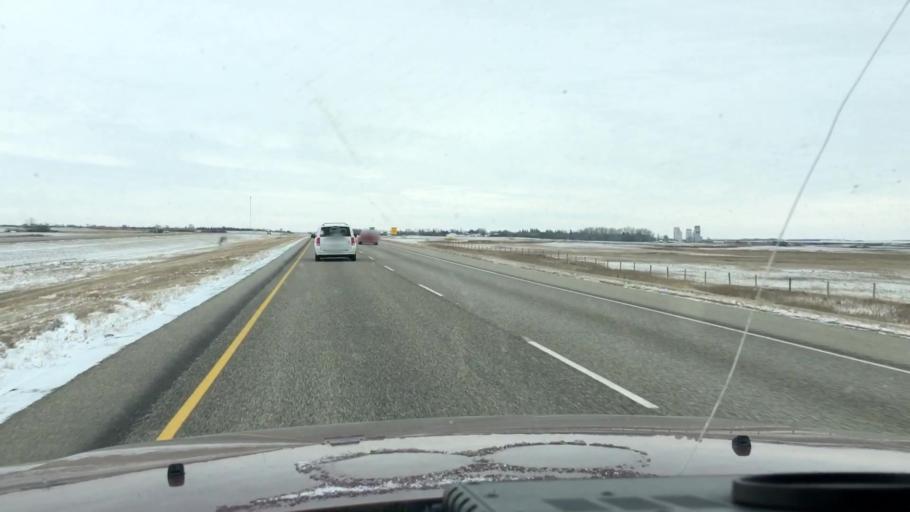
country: CA
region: Saskatchewan
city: Saskatoon
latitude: 51.5171
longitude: -106.2882
